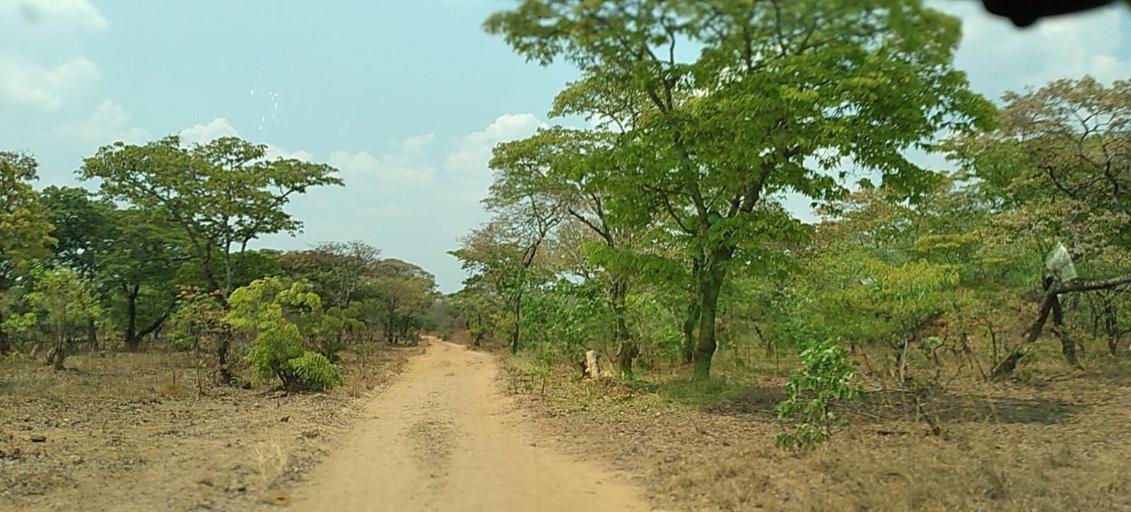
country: ZM
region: North-Western
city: Kabompo
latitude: -13.6422
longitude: 24.3803
